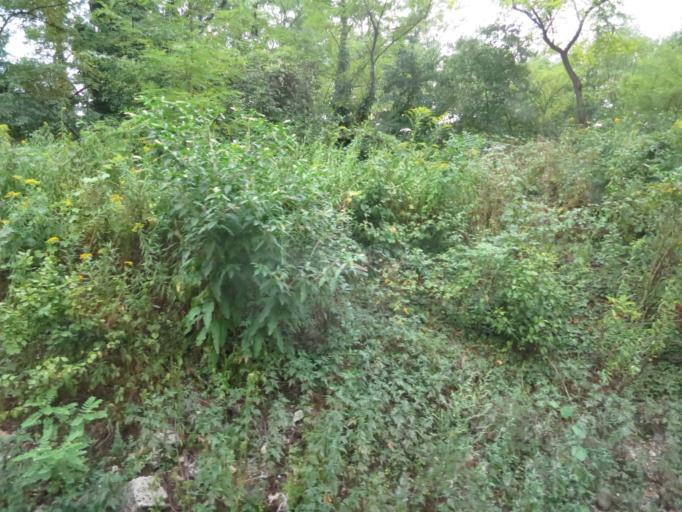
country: IT
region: Lombardy
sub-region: Provincia di Como
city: Cucciago
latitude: 45.7372
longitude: 9.0847
